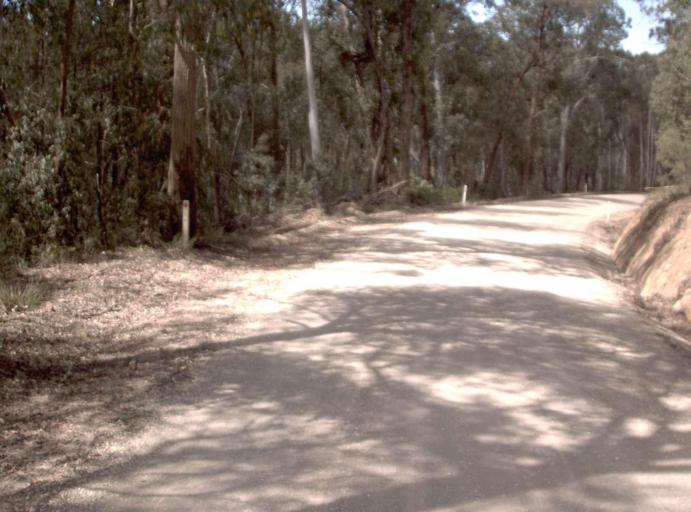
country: AU
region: New South Wales
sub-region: Bombala
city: Bombala
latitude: -37.1807
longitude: 148.7125
